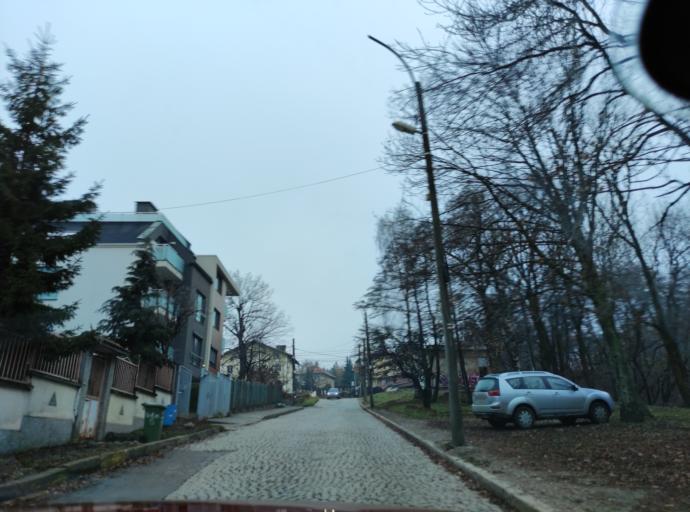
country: BG
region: Sofia-Capital
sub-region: Stolichna Obshtina
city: Sofia
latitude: 42.6266
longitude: 23.3079
